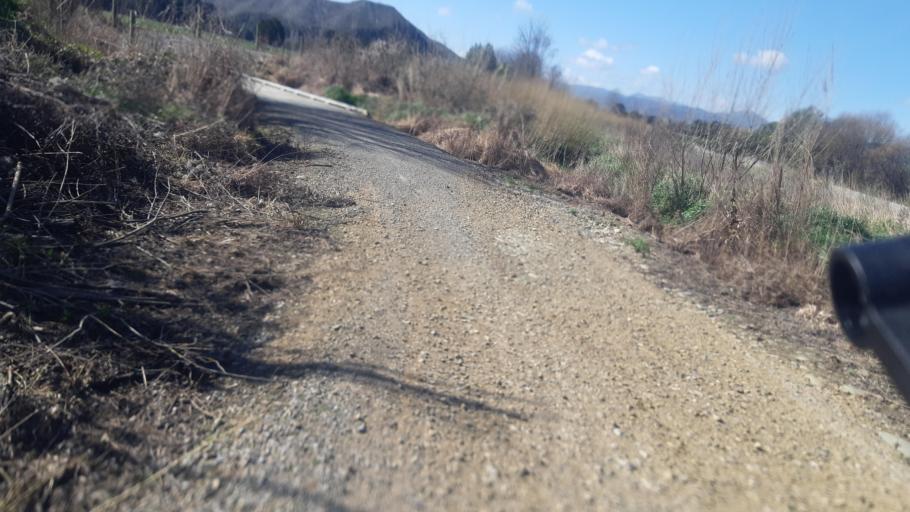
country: NZ
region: Tasman
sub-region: Tasman District
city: Wakefield
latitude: -41.4051
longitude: 173.0217
